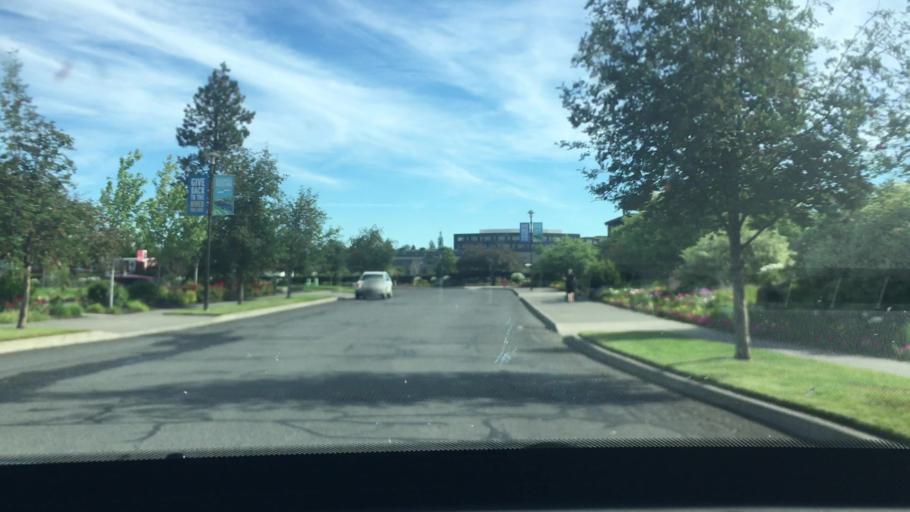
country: US
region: Oregon
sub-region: Deschutes County
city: Bend
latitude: 44.0462
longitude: -121.3192
